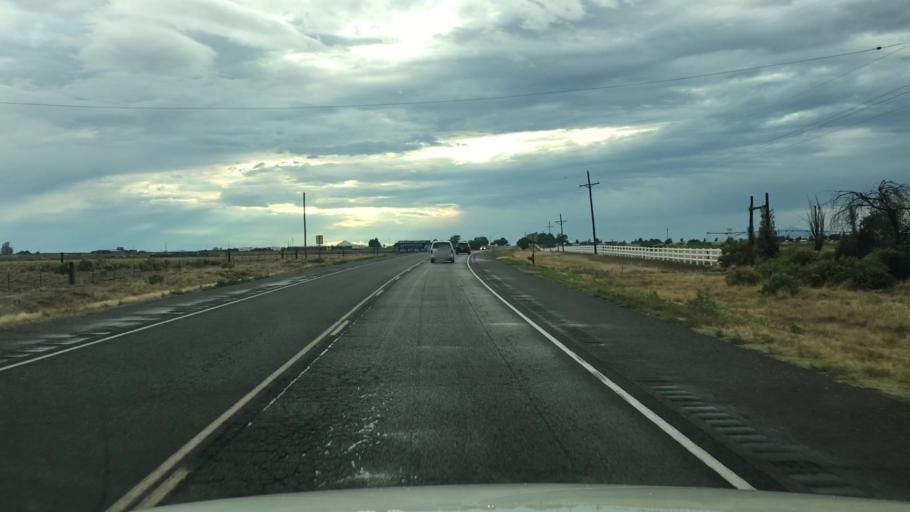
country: US
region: New Mexico
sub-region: Chaves County
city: Roswell
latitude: 33.3945
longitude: -104.4351
